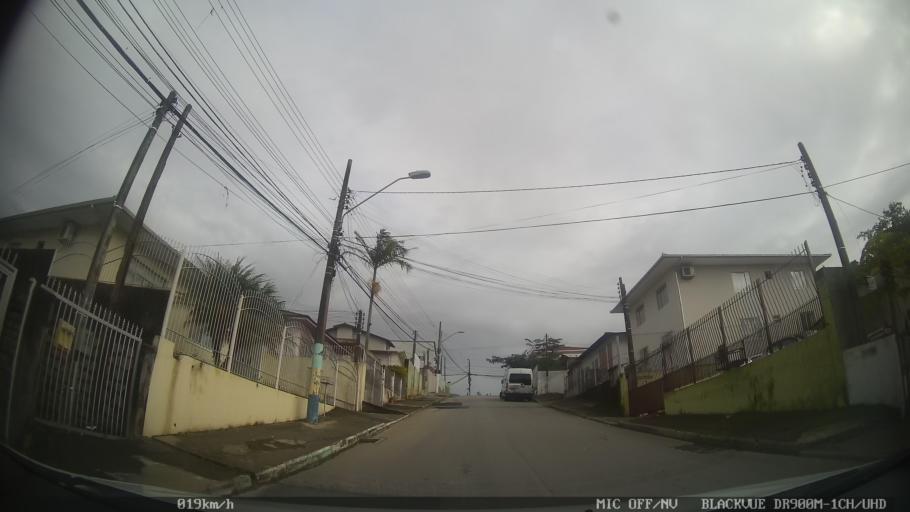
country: BR
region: Santa Catarina
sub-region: Sao Jose
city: Campinas
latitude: -27.5507
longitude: -48.6344
